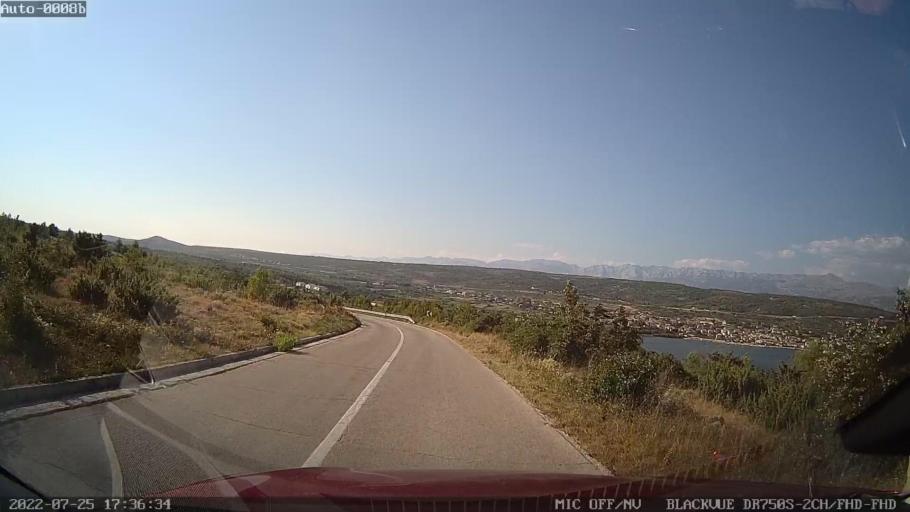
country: HR
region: Zadarska
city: Posedarje
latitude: 44.2014
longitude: 15.4710
